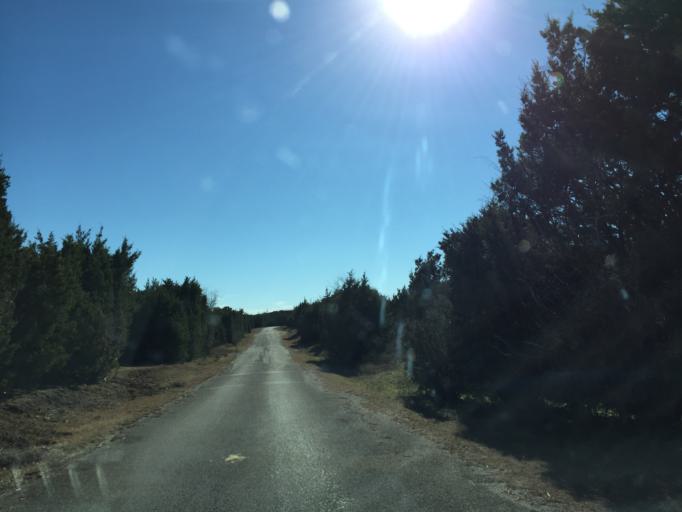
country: US
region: Texas
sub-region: Lampasas County
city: Lampasas
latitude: 30.9448
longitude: -98.1647
